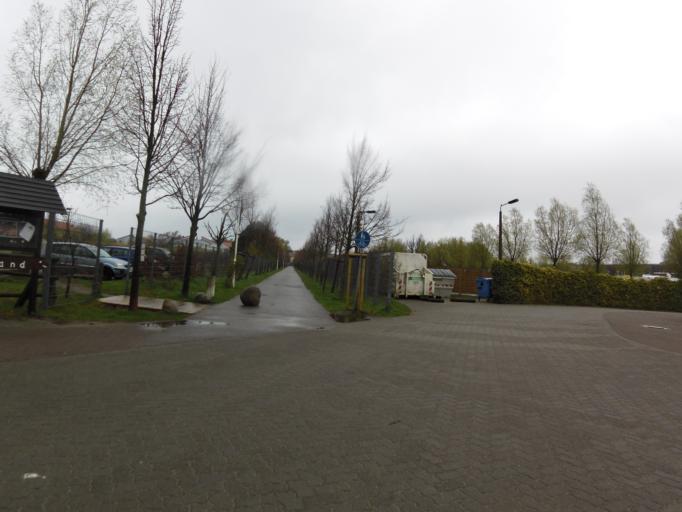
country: DE
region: Mecklenburg-Vorpommern
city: Zingst
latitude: 54.4366
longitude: 12.7057
